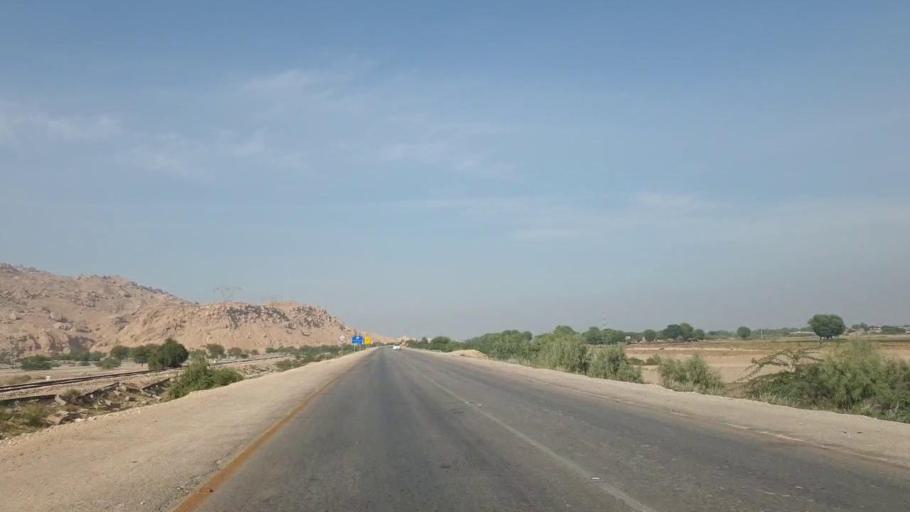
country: PK
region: Sindh
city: Sehwan
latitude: 26.2869
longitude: 67.8946
